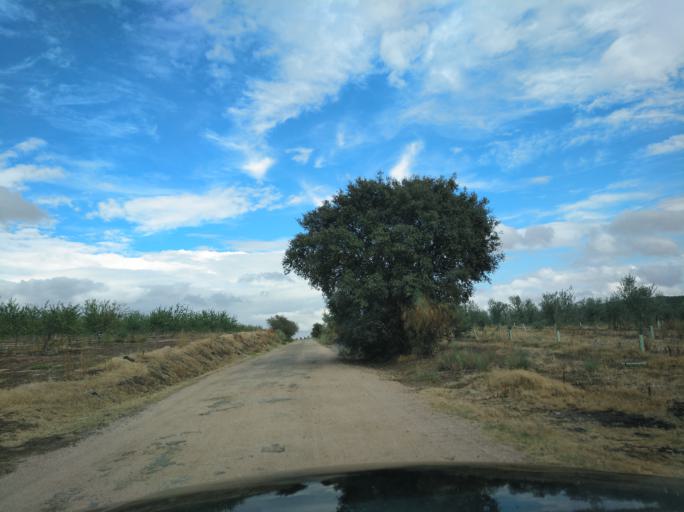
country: PT
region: Portalegre
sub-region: Campo Maior
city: Campo Maior
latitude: 39.0376
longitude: -7.1198
